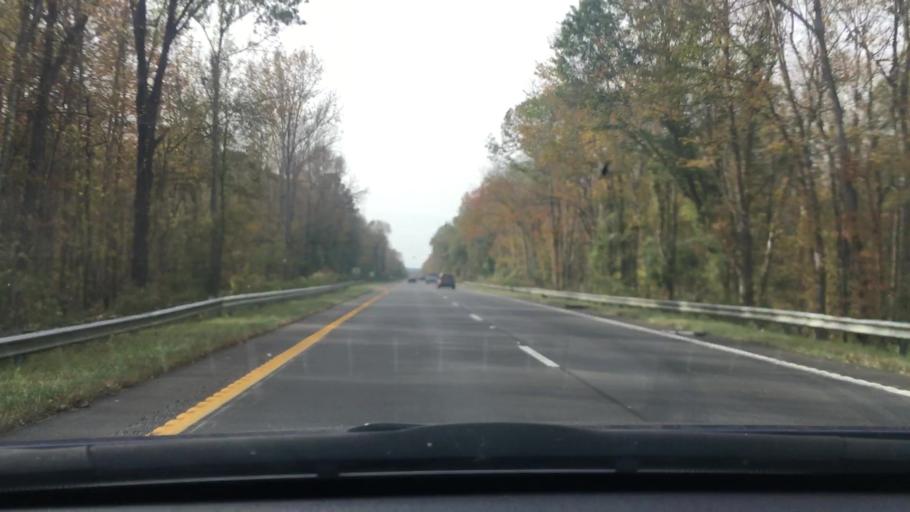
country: US
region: South Carolina
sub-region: Sumter County
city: Stateburg
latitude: 33.9522
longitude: -80.5823
